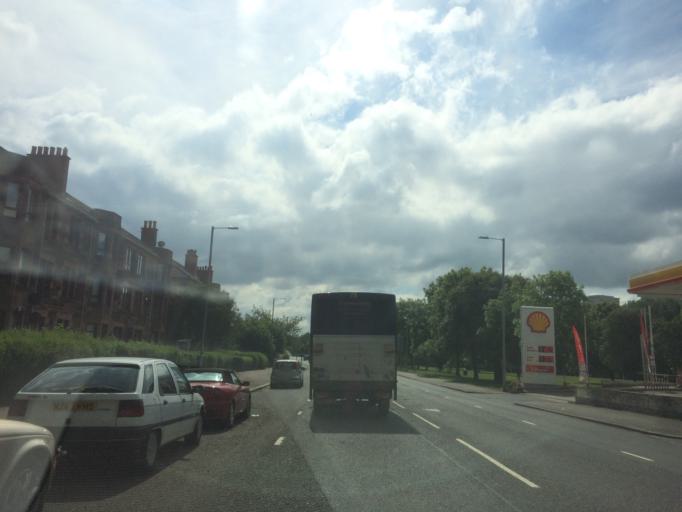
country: GB
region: Scotland
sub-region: East Renfrewshire
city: Giffnock
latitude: 55.8207
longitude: -4.3016
